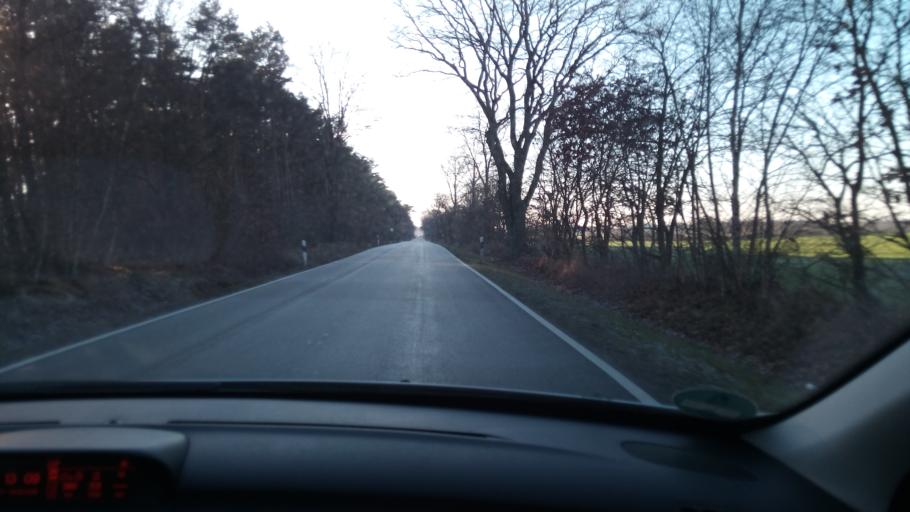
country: DE
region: Schleswig-Holstein
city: Besenthal
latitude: 53.5346
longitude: 10.7245
